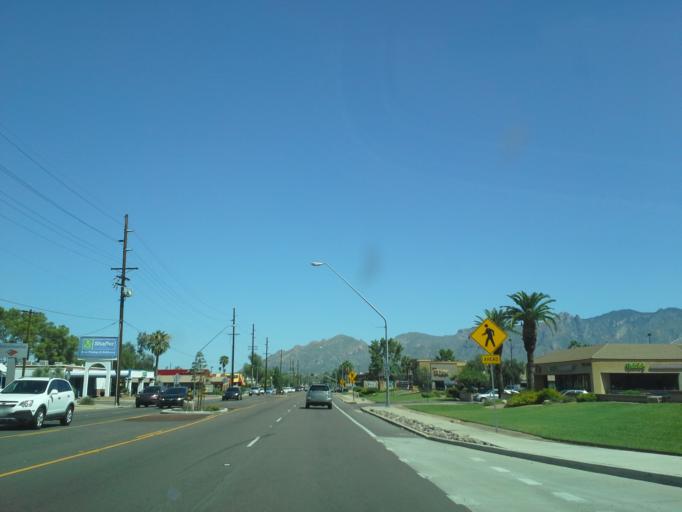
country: US
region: Arizona
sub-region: Pima County
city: Tucson
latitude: 32.2586
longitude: -110.9438
